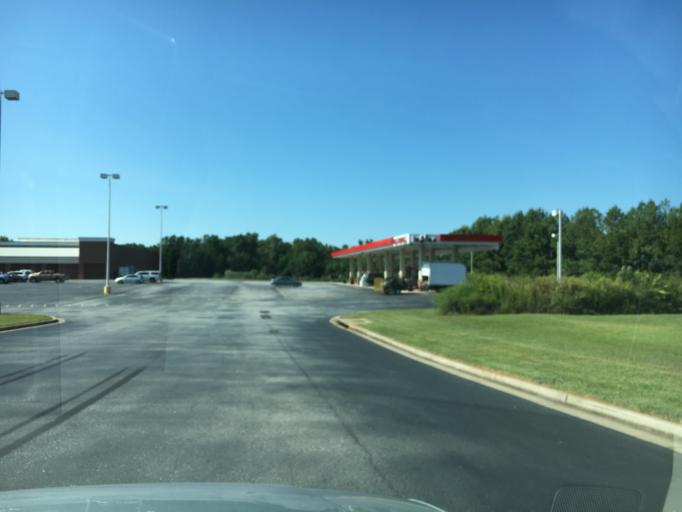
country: US
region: South Carolina
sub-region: Spartanburg County
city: Wellford
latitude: 34.8884
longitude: -82.0714
